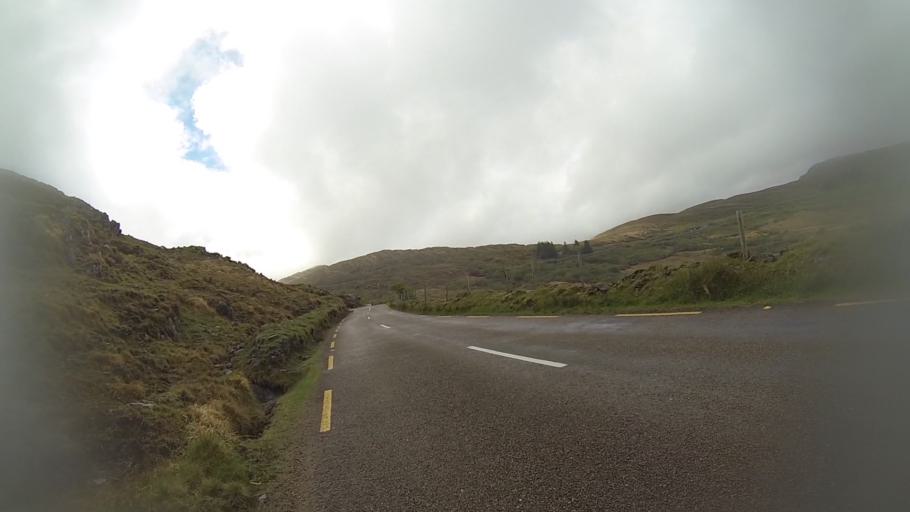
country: IE
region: Munster
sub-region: Ciarrai
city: Killorglin
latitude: 51.8751
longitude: -9.8121
